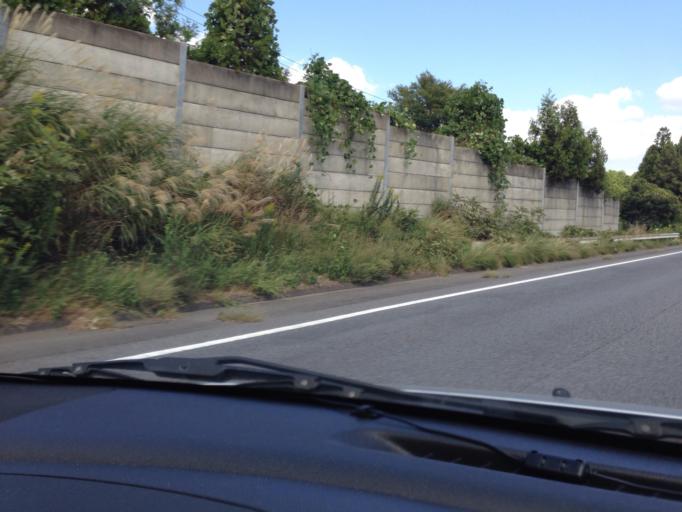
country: JP
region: Ibaraki
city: Ishioka
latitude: 36.1624
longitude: 140.2322
